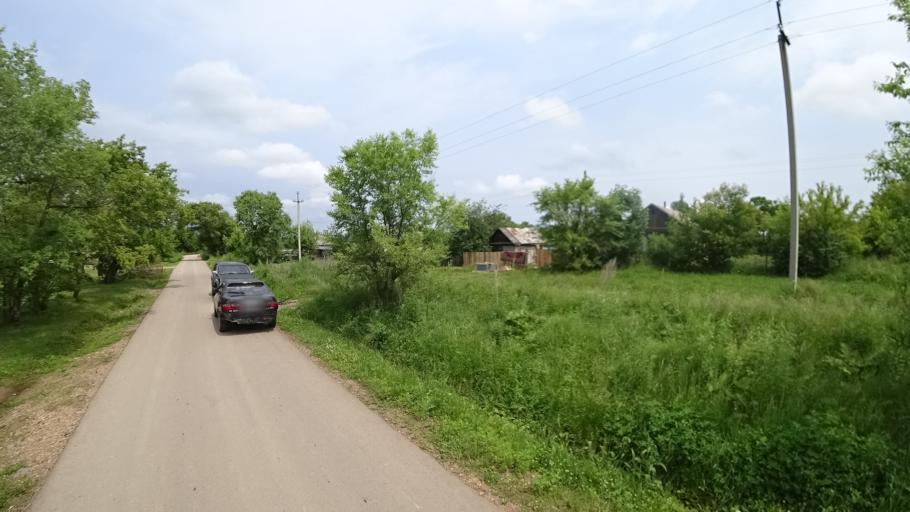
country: RU
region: Primorskiy
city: Novosysoyevka
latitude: 44.2377
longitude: 133.3583
